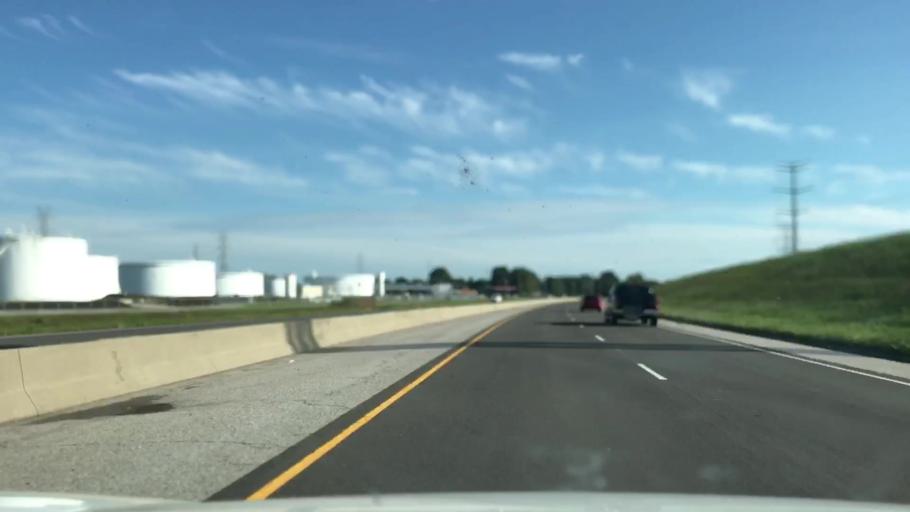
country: US
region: Illinois
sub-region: Madison County
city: Hartford
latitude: 38.8458
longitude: -90.0988
